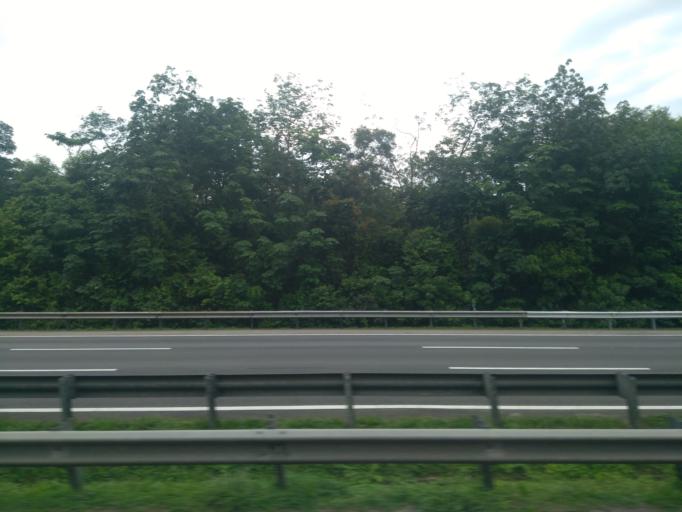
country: MY
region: Melaka
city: Alor Gajah
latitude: 2.4062
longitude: 102.2186
